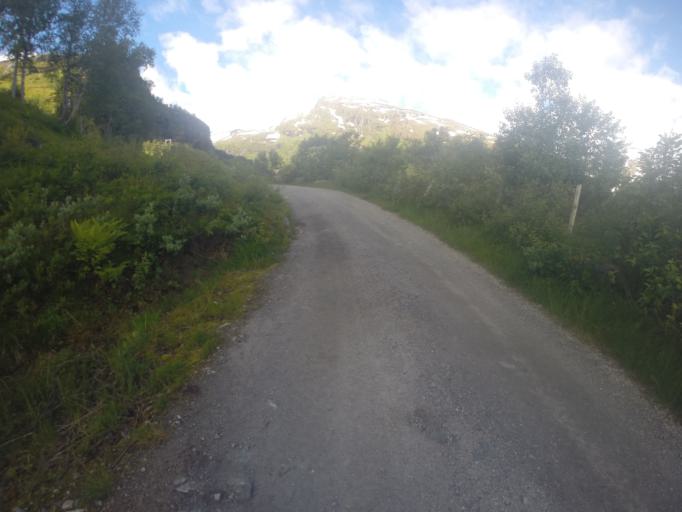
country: NO
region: Sogn og Fjordane
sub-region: Aurland
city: Aurlandsvangen
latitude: 60.7433
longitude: 7.1288
